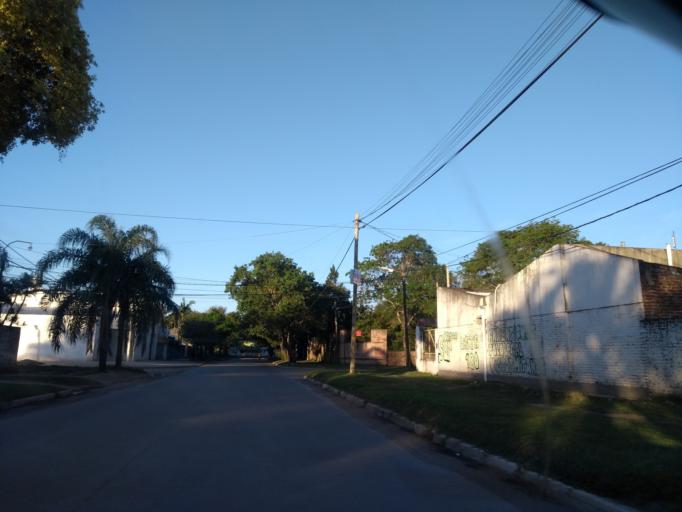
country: AR
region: Chaco
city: Resistencia
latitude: -27.4682
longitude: -58.9610
